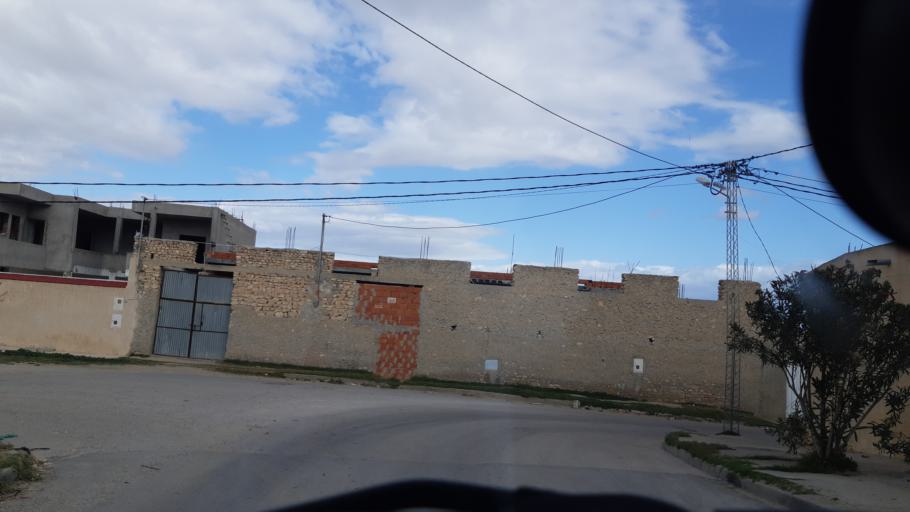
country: TN
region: Susah
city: Akouda
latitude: 35.8685
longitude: 10.5179
